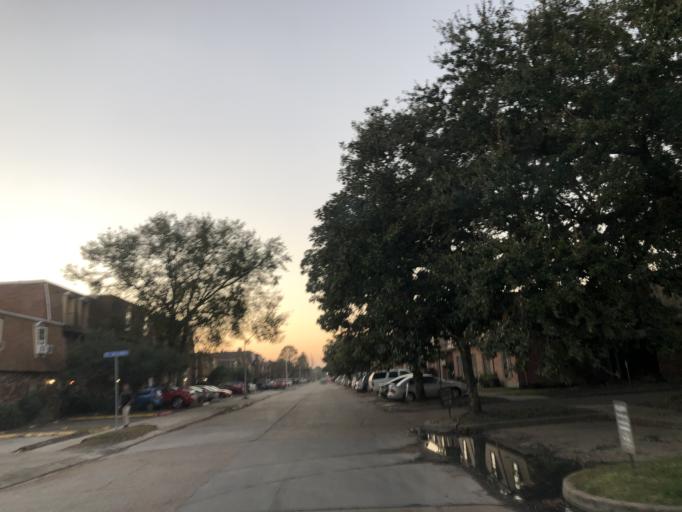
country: US
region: Louisiana
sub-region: Jefferson Parish
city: Kenner
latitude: 30.0090
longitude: -90.2120
